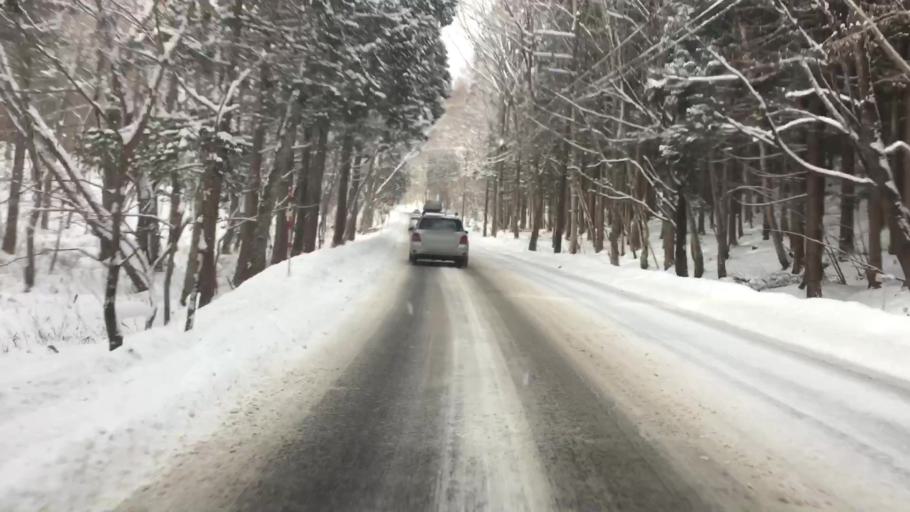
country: JP
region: Tochigi
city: Yaita
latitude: 36.9536
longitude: 139.7604
